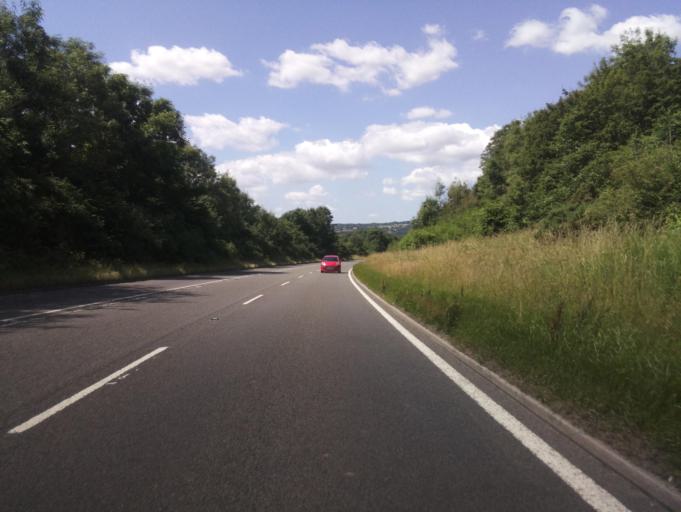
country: GB
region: England
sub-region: Derbyshire
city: Ashbourne
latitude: 53.0041
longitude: -1.7289
